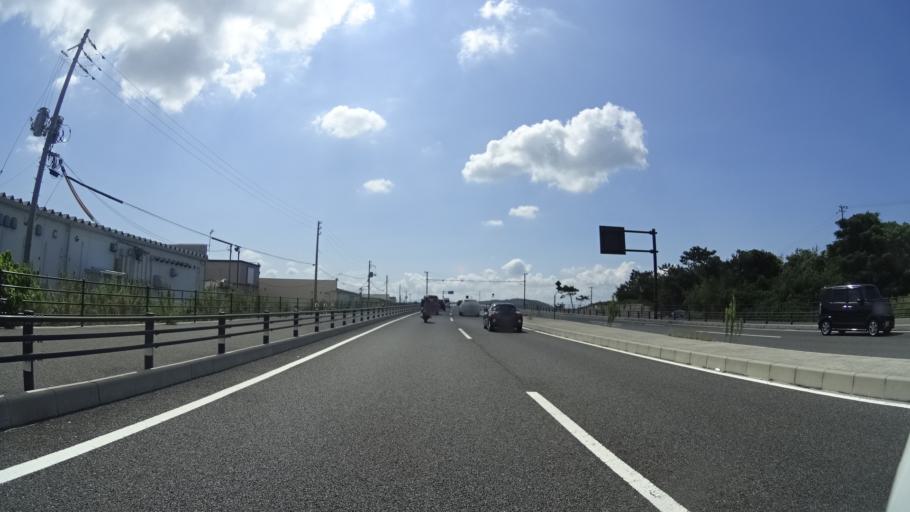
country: JP
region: Yamaguchi
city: Shimonoseki
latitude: 34.0201
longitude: 130.9174
